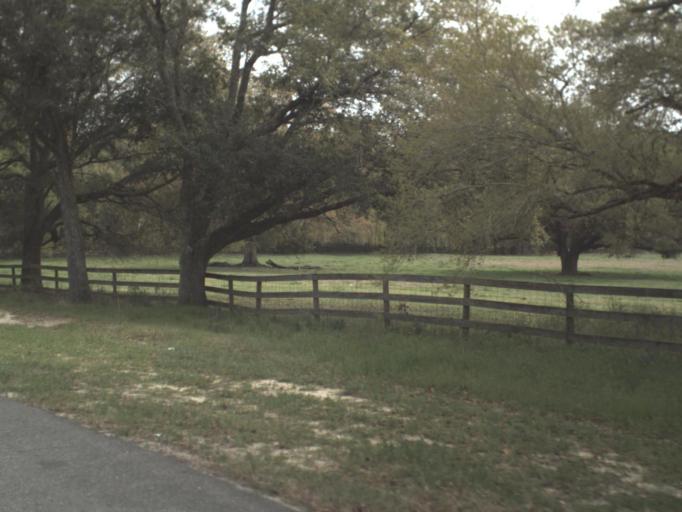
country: US
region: Florida
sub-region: Holmes County
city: Bonifay
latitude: 30.8692
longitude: -85.6651
